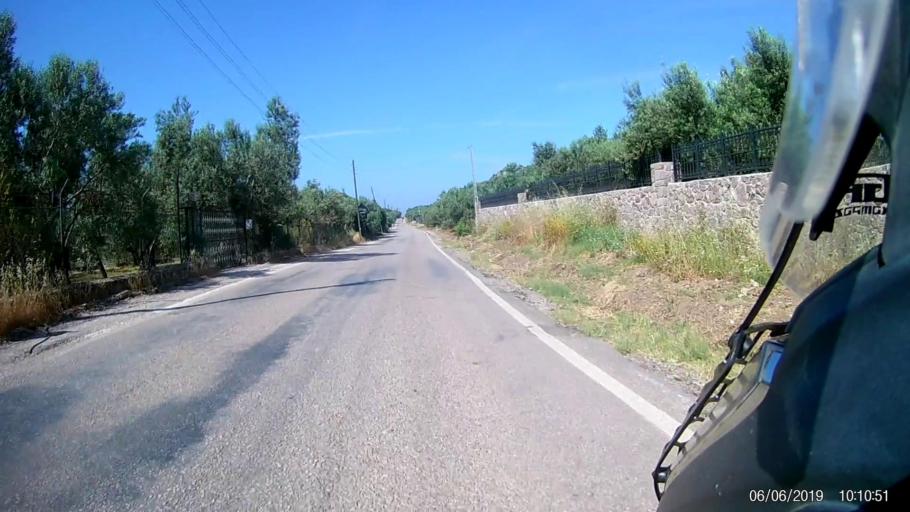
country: TR
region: Canakkale
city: Ayvacik
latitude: 39.5144
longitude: 26.4364
